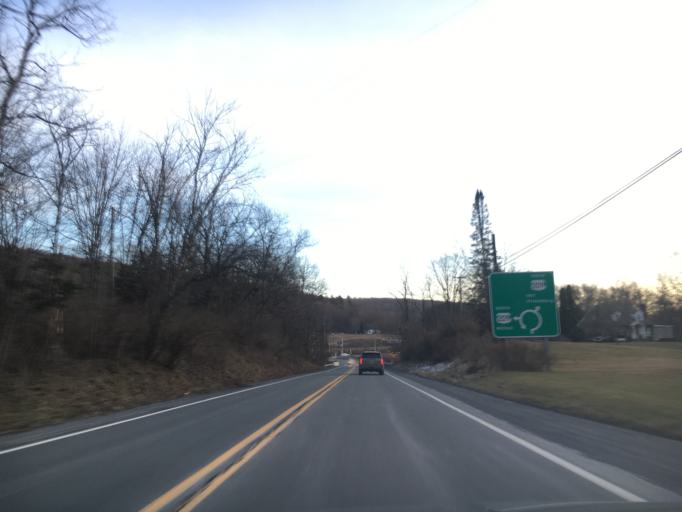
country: US
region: Pennsylvania
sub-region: Monroe County
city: East Stroudsburg
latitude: 41.0362
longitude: -75.1250
